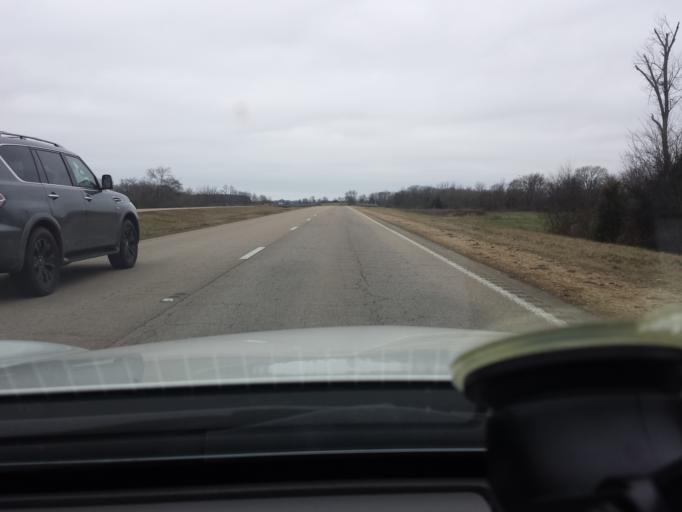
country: US
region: Mississippi
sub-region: Lee County
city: Shannon
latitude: 34.0787
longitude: -88.7015
